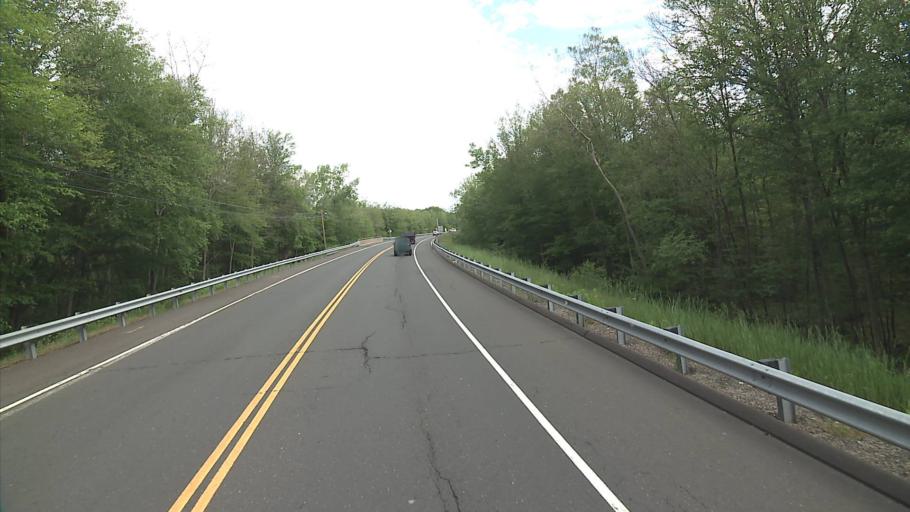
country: US
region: Connecticut
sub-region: New Haven County
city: Naugatuck
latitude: 41.5209
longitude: -73.0812
